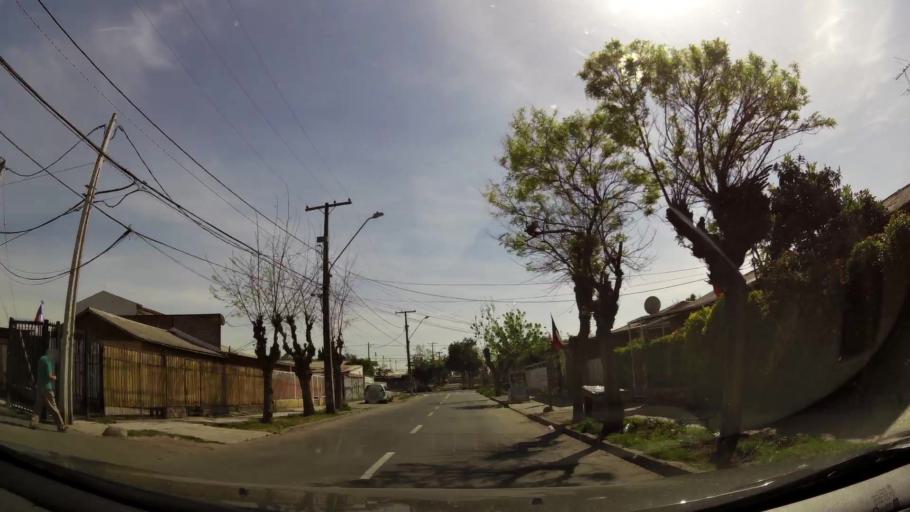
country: CL
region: Santiago Metropolitan
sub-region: Provincia de Cordillera
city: Puente Alto
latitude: -33.6190
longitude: -70.5892
